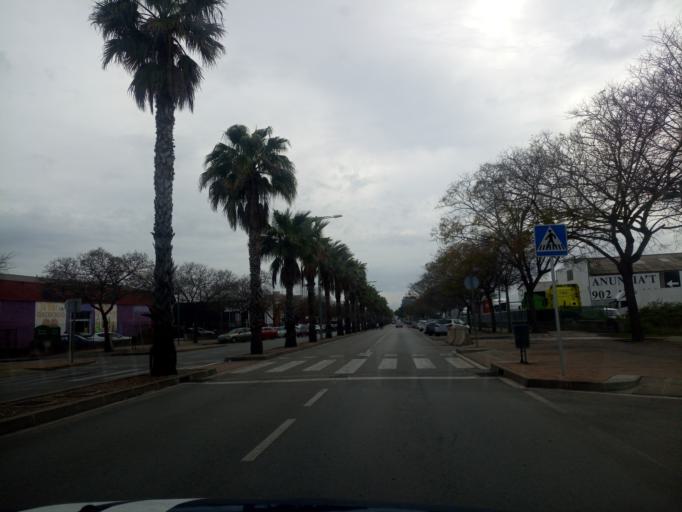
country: ES
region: Catalonia
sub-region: Provincia de Barcelona
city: Vilanova i la Geltru
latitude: 41.2274
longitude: 1.7586
